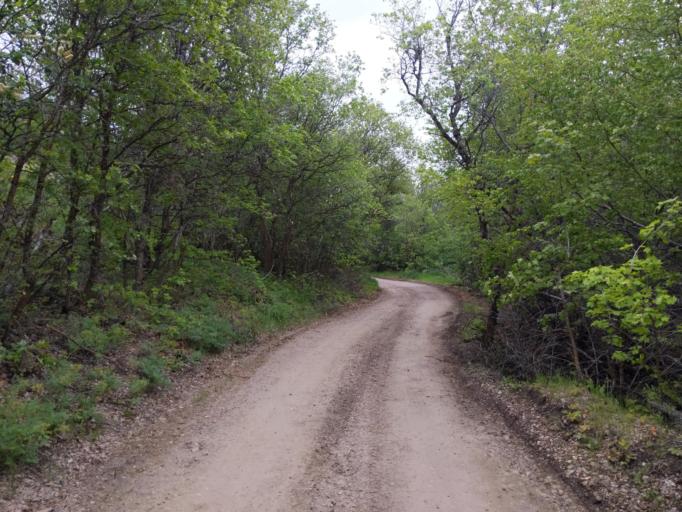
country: US
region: Idaho
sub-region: Bannock County
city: Pocatello
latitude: 42.8310
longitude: -112.4796
